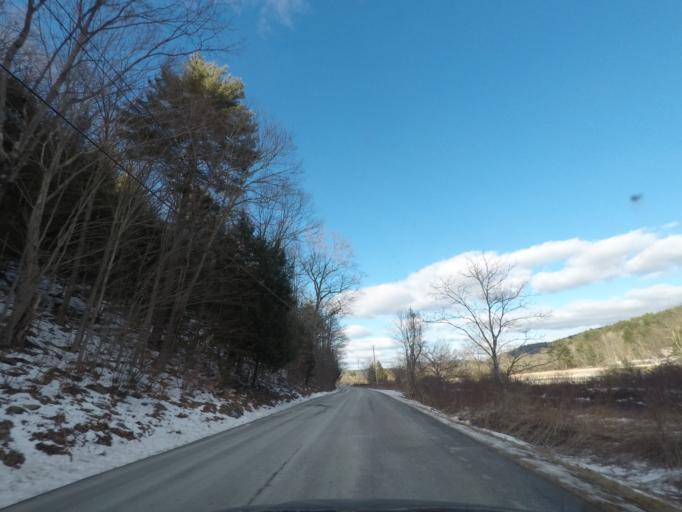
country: US
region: New York
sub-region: Rensselaer County
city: Nassau
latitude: 42.5377
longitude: -73.5294
